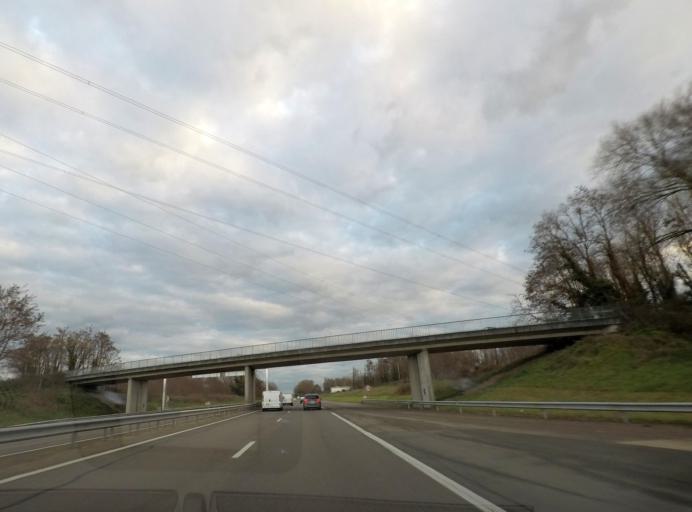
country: FR
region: Rhone-Alpes
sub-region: Departement de l'Ain
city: Crottet
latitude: 46.2946
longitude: 4.9092
